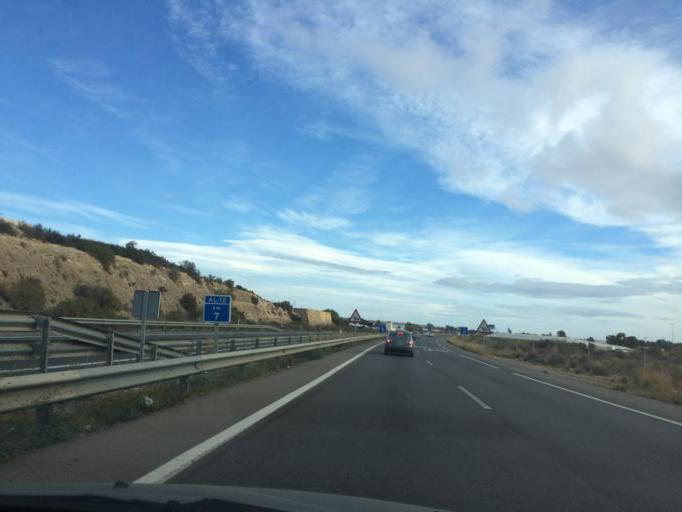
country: ES
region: Andalusia
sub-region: Provincia de Almeria
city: Viator
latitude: 36.8475
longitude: -2.3871
